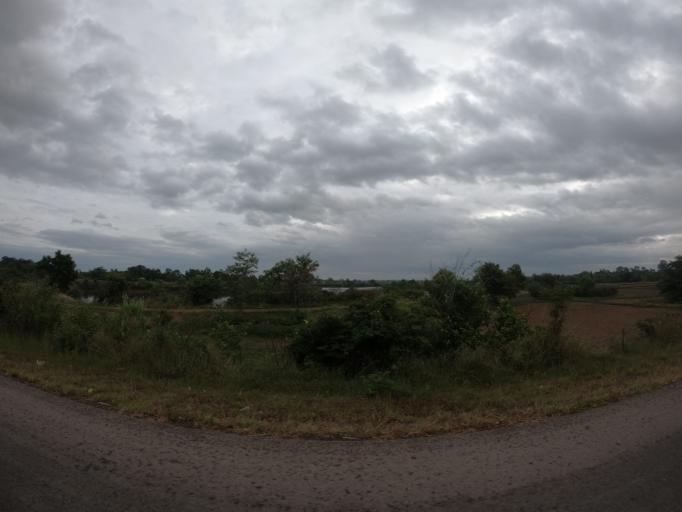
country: TH
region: Roi Et
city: Chiang Khwan
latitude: 16.1213
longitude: 103.8458
